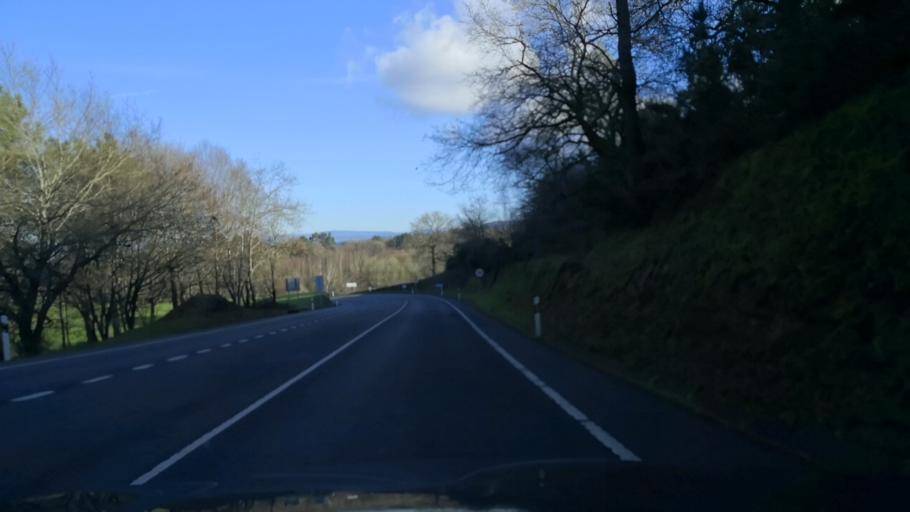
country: ES
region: Galicia
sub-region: Provincia de Pontevedra
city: Silleda
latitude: 42.6976
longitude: -8.3276
